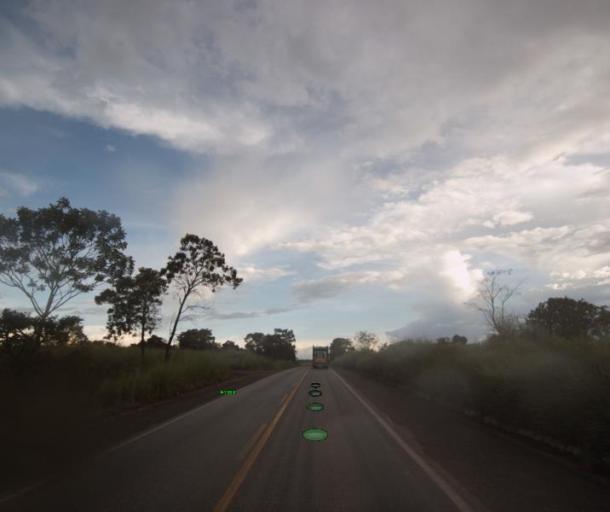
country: BR
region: Goias
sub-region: Uruacu
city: Uruacu
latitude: -13.9871
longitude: -49.0906
